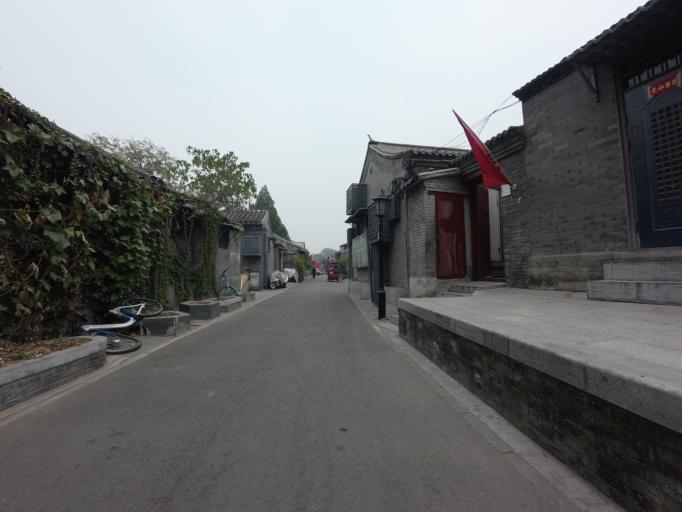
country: CN
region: Beijing
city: Jingshan
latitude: 39.9375
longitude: 116.3849
